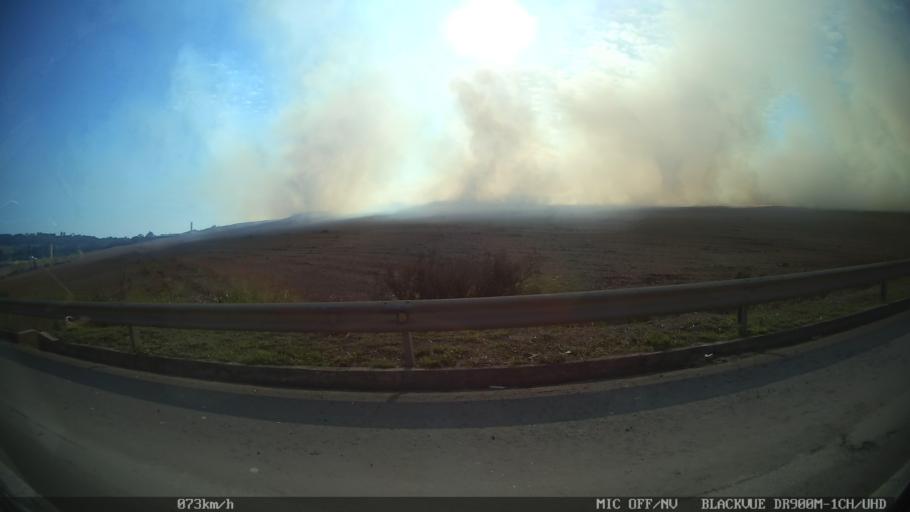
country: BR
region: Sao Paulo
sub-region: Piracicaba
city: Piracicaba
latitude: -22.6961
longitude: -47.6048
